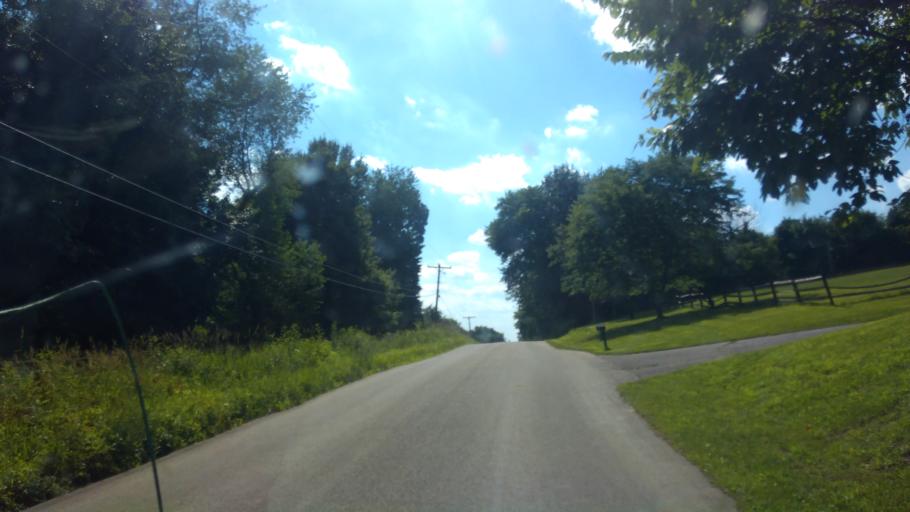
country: US
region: Ohio
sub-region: Stark County
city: Brewster
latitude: 40.7296
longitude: -81.6417
